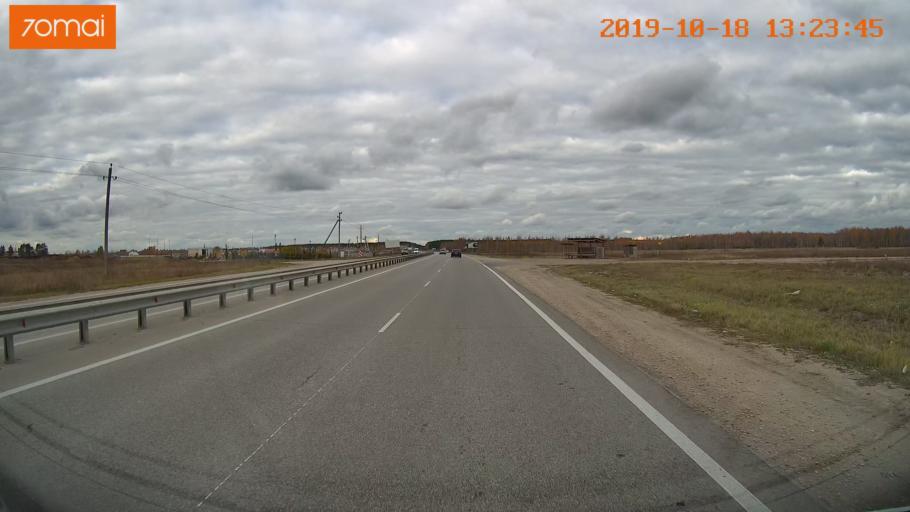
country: RU
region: Rjazan
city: Polyany
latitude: 54.7210
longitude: 39.8477
